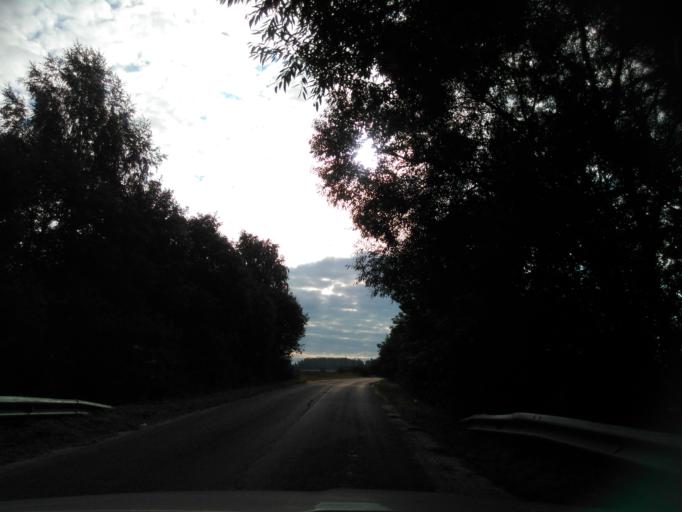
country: RU
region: Moskovskaya
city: Peshki
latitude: 56.1269
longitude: 37.0184
